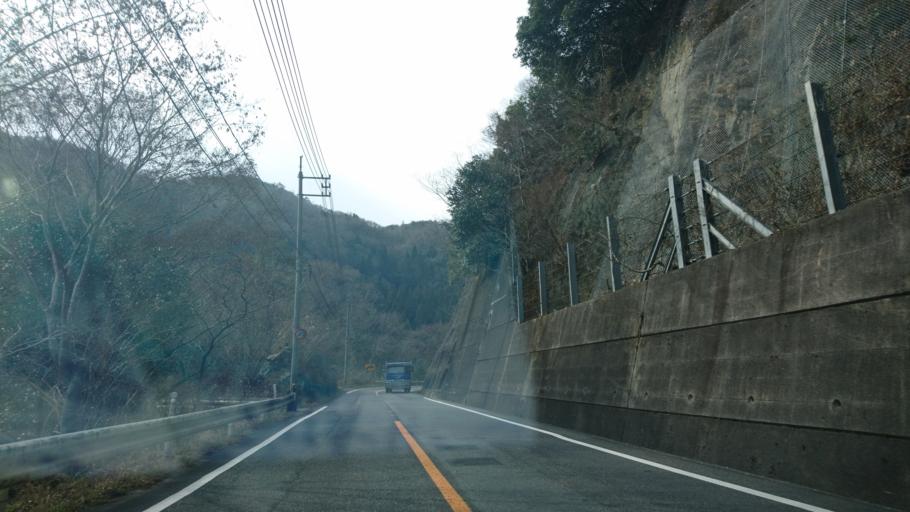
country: JP
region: Okayama
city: Takahashi
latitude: 34.8225
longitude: 133.6617
